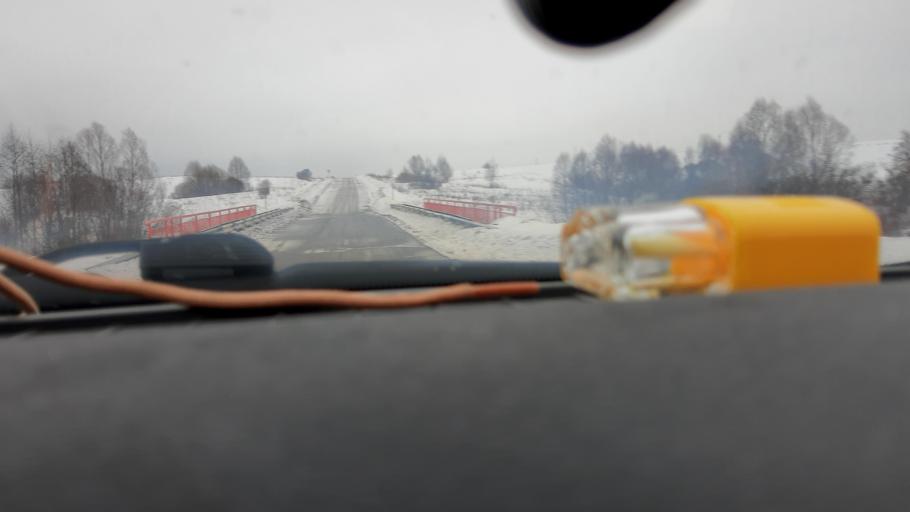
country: RU
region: Bashkortostan
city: Iglino
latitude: 54.6403
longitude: 56.4233
